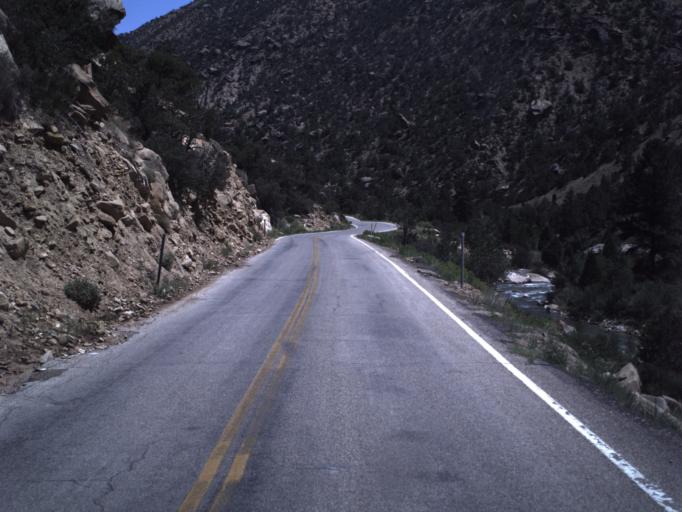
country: US
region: Utah
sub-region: Emery County
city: Orangeville
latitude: 39.2741
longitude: -111.2035
